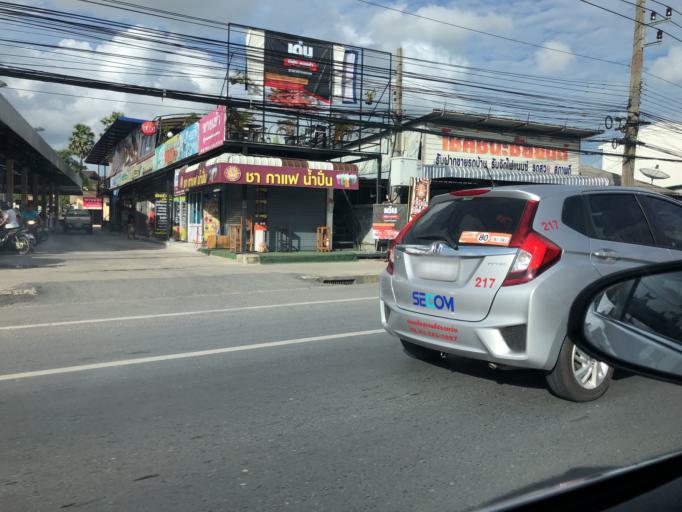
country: TH
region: Phuket
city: Thalang
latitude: 8.0048
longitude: 98.3443
